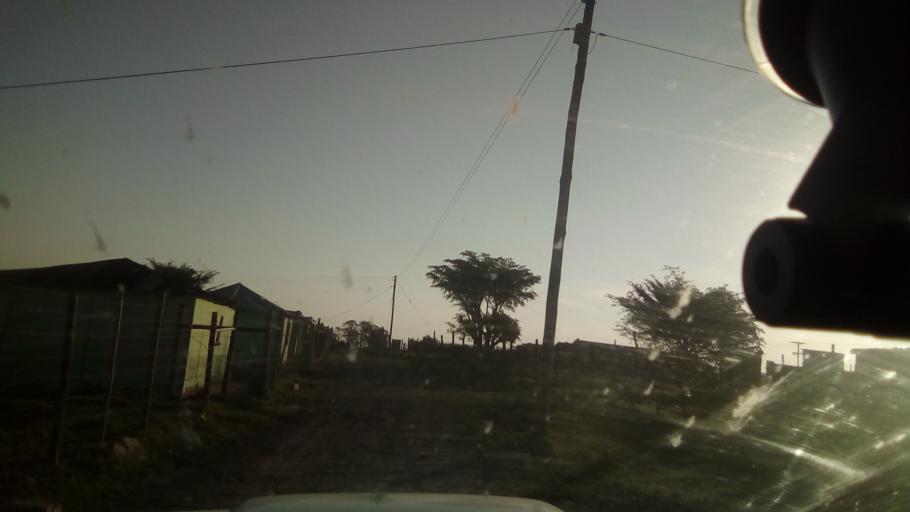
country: ZA
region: Eastern Cape
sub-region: Buffalo City Metropolitan Municipality
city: Bhisho
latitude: -32.9726
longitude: 27.2954
